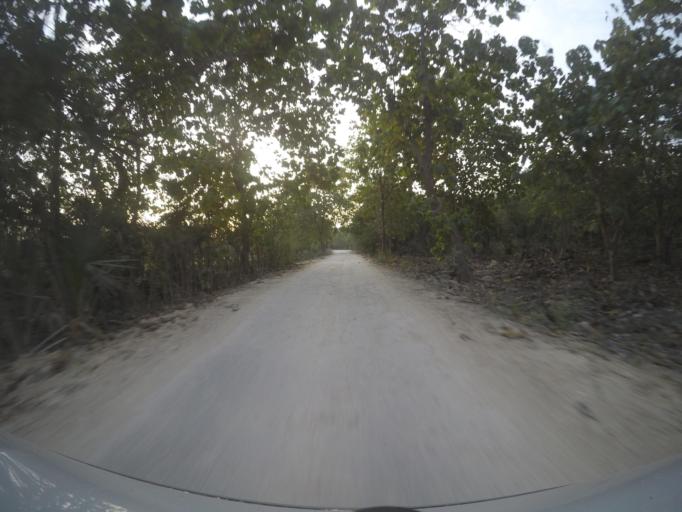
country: TL
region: Viqueque
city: Viqueque
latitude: -8.9389
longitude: 126.4181
